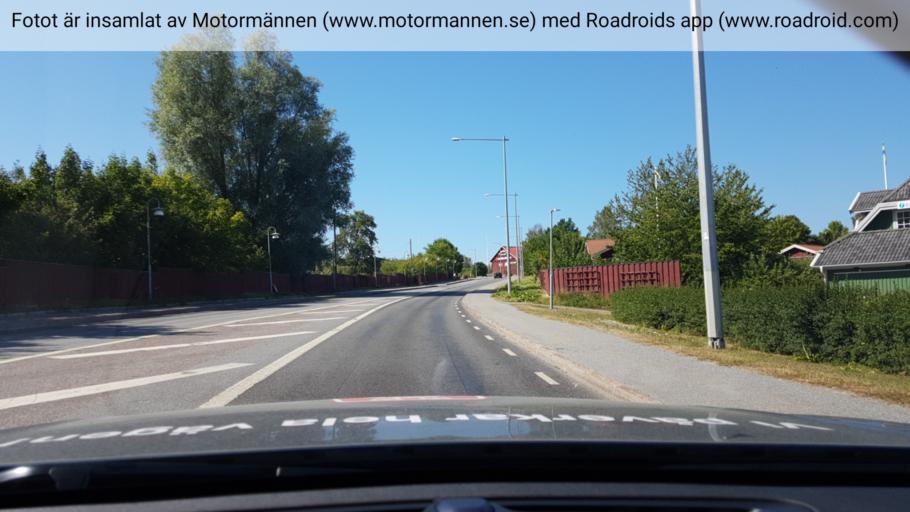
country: SE
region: Stockholm
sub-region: Ekero Kommun
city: Ekeroe
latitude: 59.2787
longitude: 17.7892
